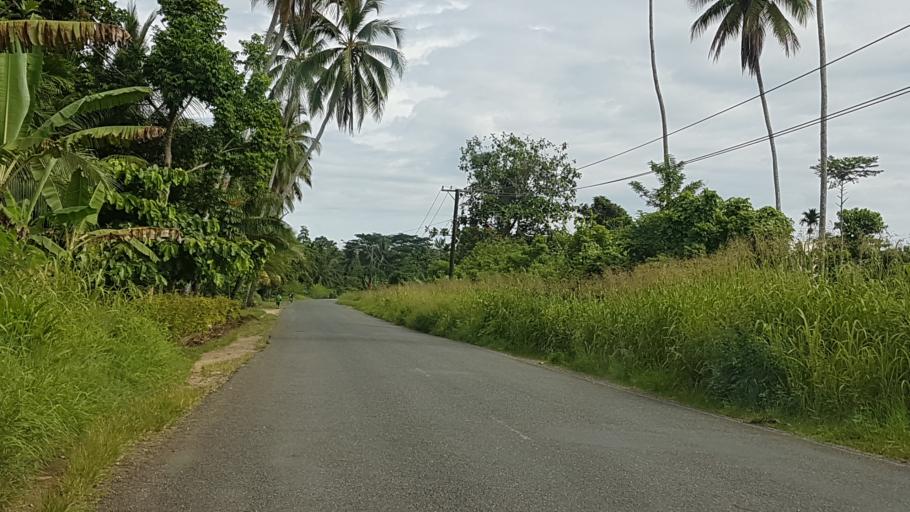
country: PG
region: Madang
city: Madang
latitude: -5.1864
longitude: 145.7758
